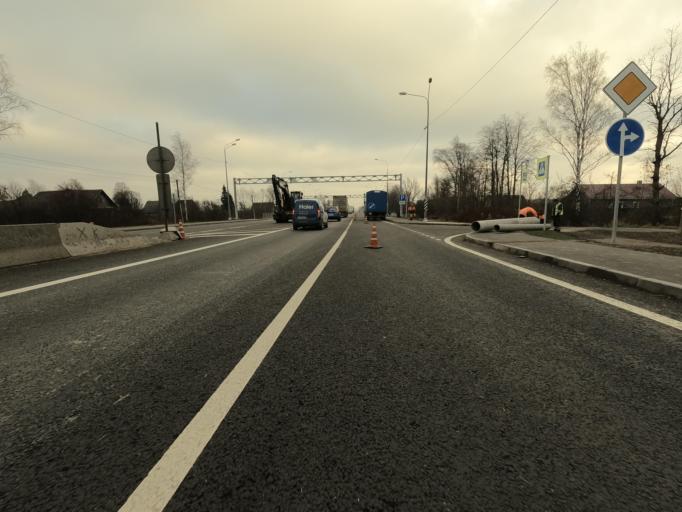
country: RU
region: Leningrad
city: Mga
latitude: 59.7219
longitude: 31.0990
